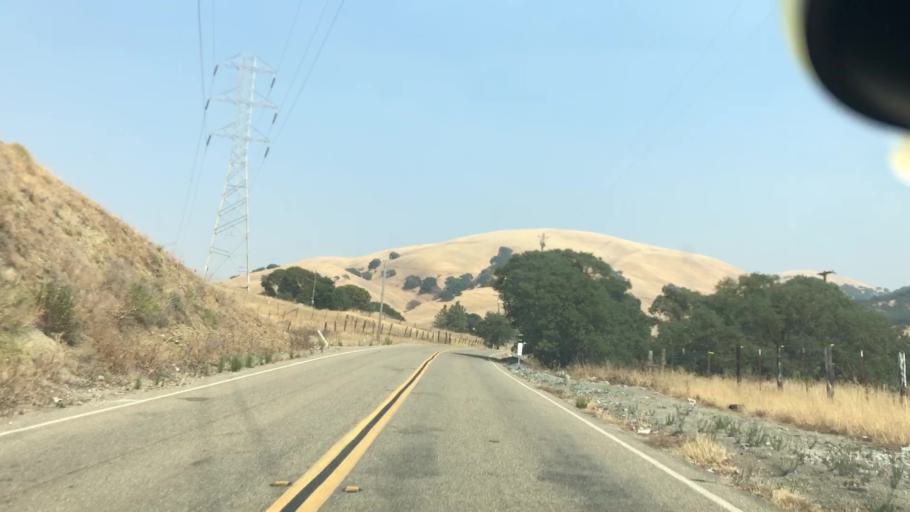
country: US
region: California
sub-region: Alameda County
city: Livermore
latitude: 37.6431
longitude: -121.6446
